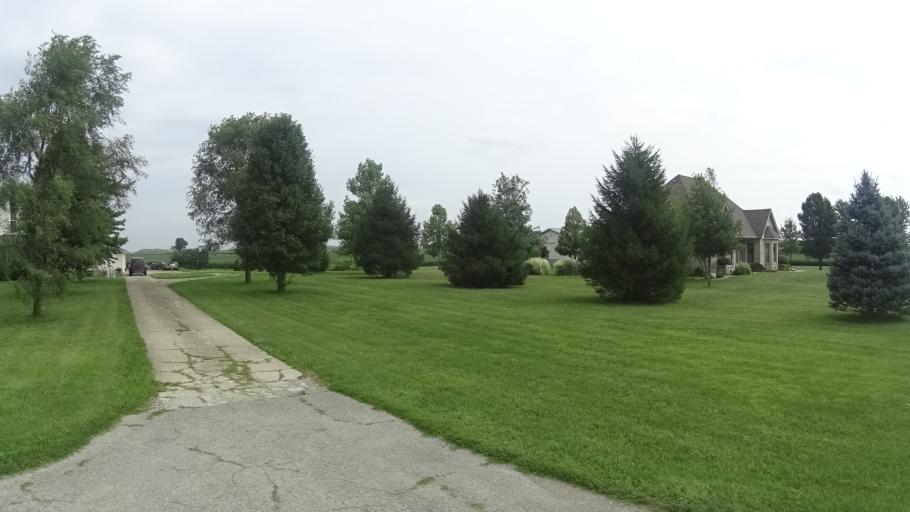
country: US
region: Indiana
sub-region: Madison County
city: Lapel
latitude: 40.0362
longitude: -85.7972
